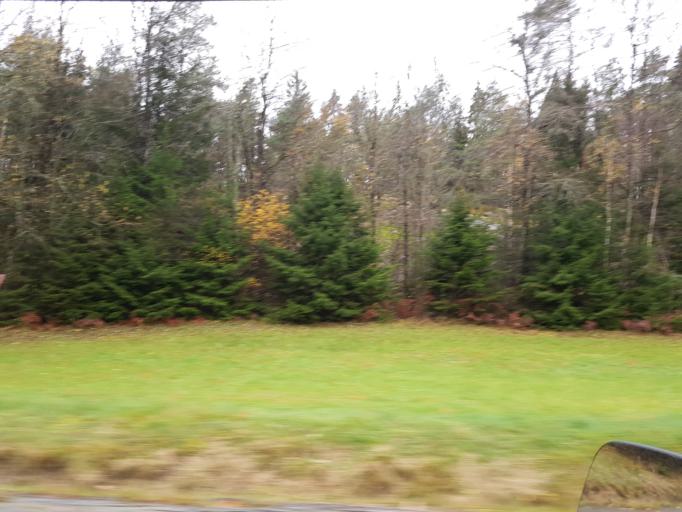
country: SE
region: Vaestra Goetaland
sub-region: Orust
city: Henan
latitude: 58.2339
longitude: 11.7322
